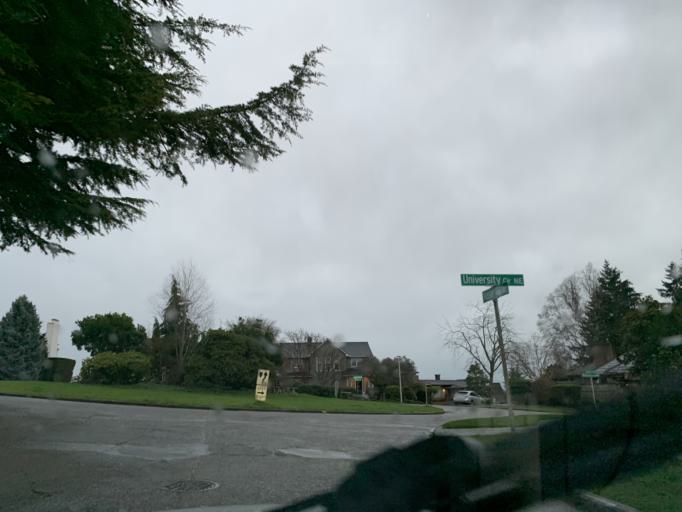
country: US
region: Washington
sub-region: King County
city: Yarrow Point
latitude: 47.6720
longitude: -122.2759
